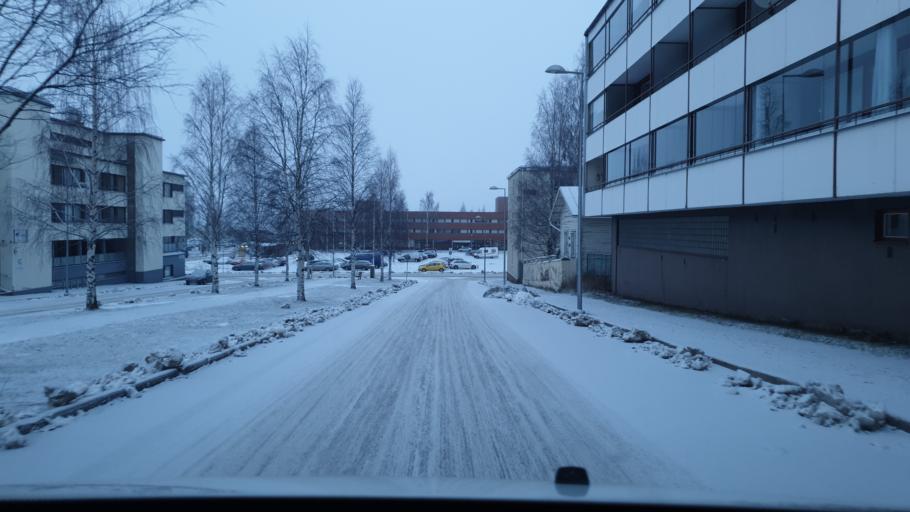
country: FI
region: Lapland
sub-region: Kemi-Tornio
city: Kemi
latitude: 65.7341
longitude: 24.5614
